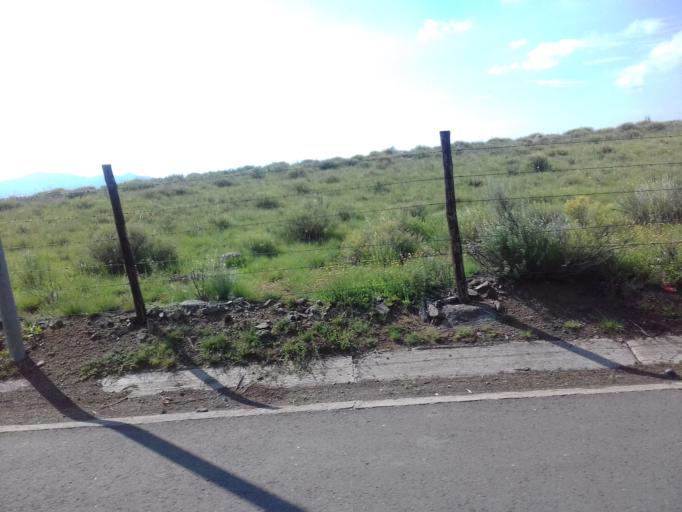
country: LS
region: Thaba-Tseka
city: Thaba-Tseka
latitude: -29.5190
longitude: 28.6182
